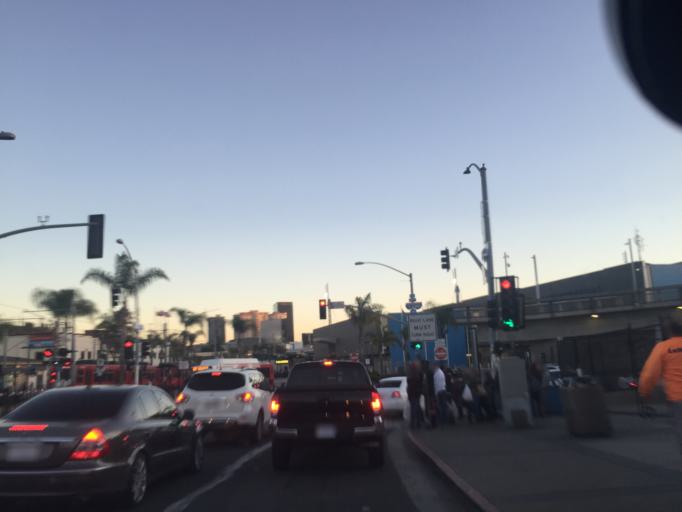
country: MX
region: Baja California
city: Tijuana
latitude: 32.5450
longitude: -117.0303
